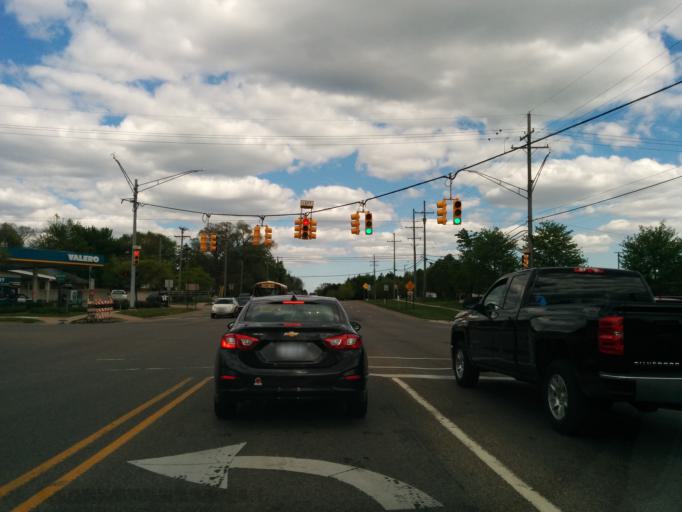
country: US
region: Michigan
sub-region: Oakland County
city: Farmington Hills
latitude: 42.4997
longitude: -83.3396
